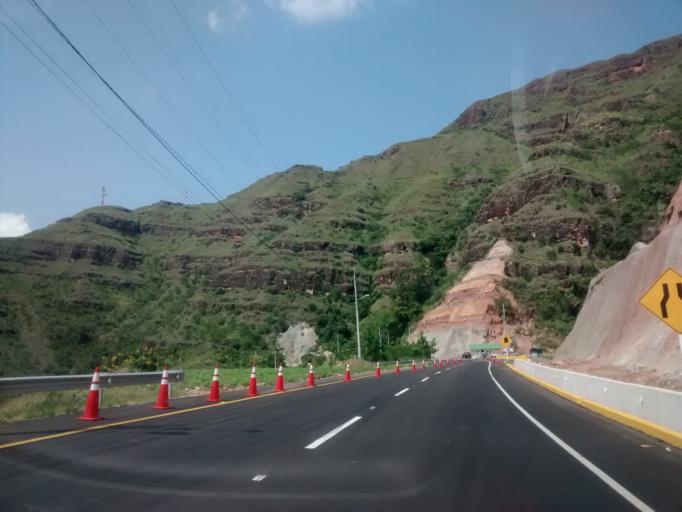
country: CO
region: Tolima
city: Valle de San Juan
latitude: 4.2846
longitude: -75.0216
